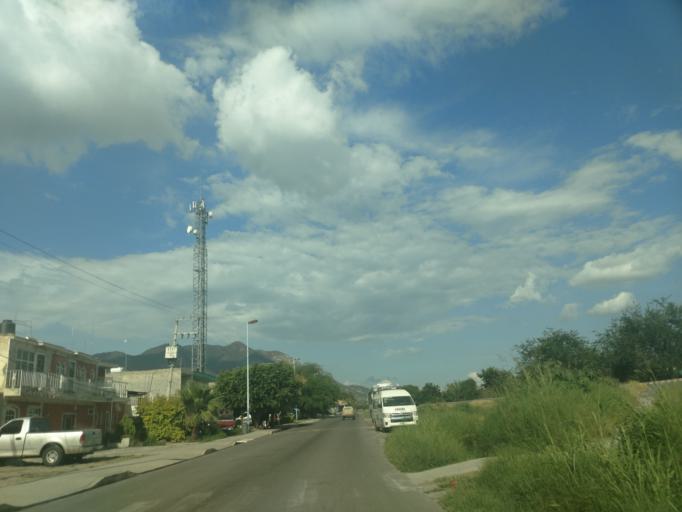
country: MX
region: Jalisco
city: Antonio Escobedo
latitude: 20.9060
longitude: -103.9797
